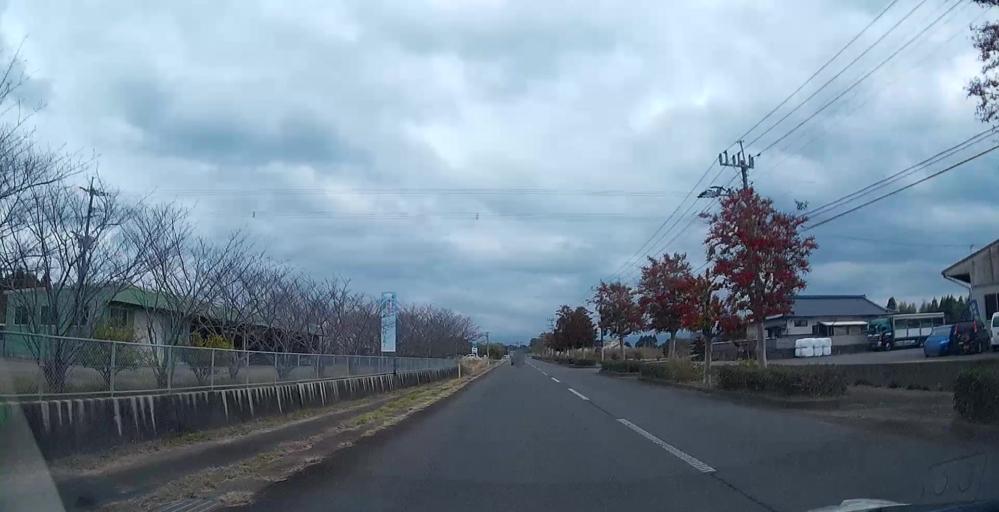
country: JP
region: Kagoshima
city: Akune
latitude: 32.0763
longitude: 130.2088
